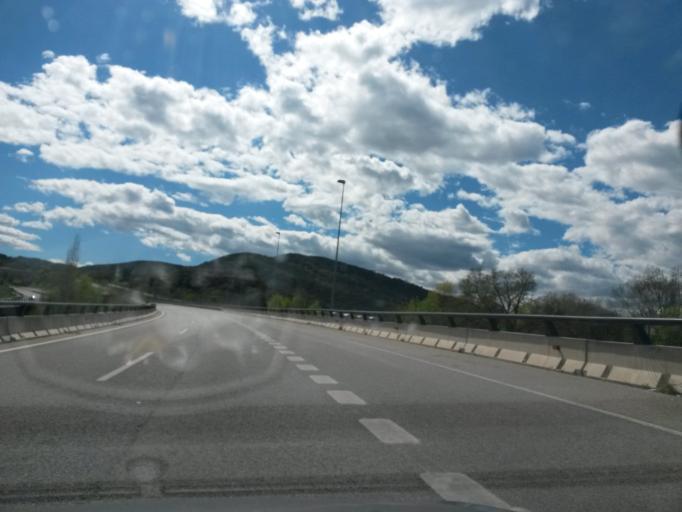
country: ES
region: Catalonia
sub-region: Provincia de Girona
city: Sant Joan les Fonts
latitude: 42.2142
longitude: 2.5419
